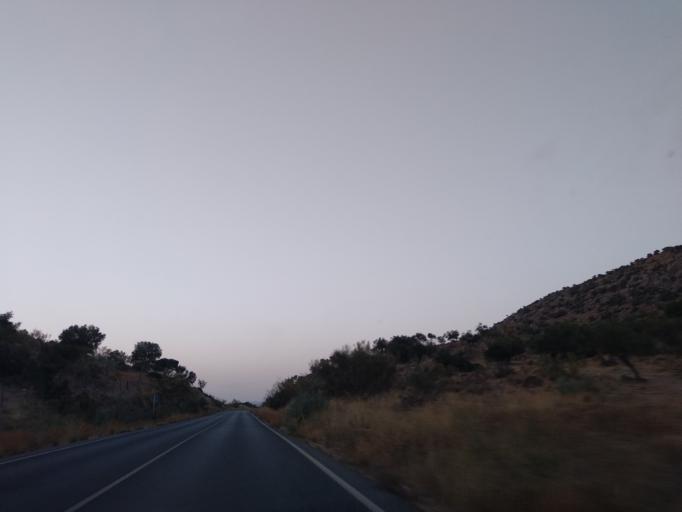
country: ES
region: Andalusia
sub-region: Provincia de Malaga
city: Cartama
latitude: 36.6935
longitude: -4.6511
